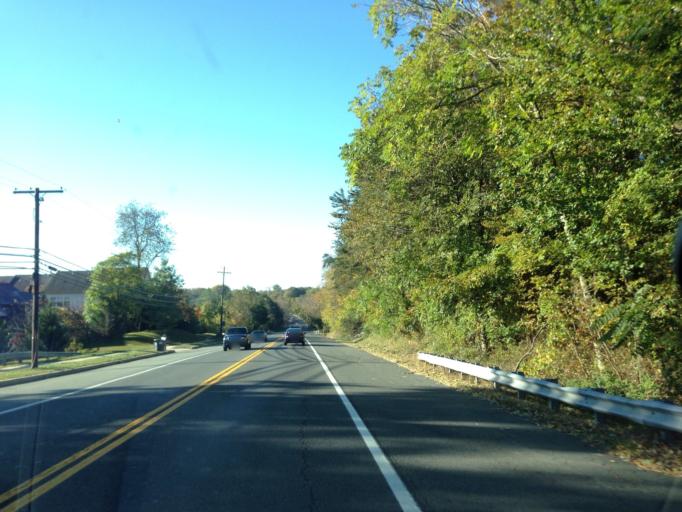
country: US
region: Maryland
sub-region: Montgomery County
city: Damascus
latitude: 39.2728
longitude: -77.2159
